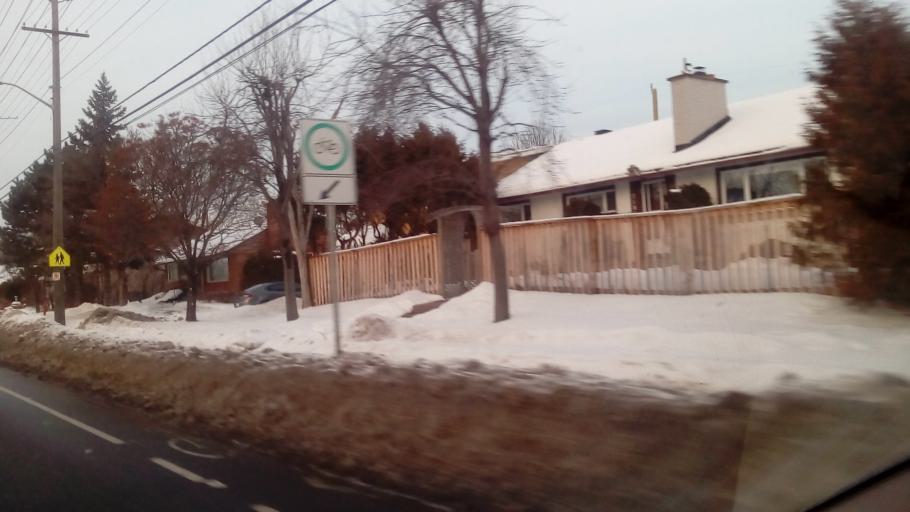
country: CA
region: Ontario
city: Ottawa
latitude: 45.3907
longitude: -75.6184
